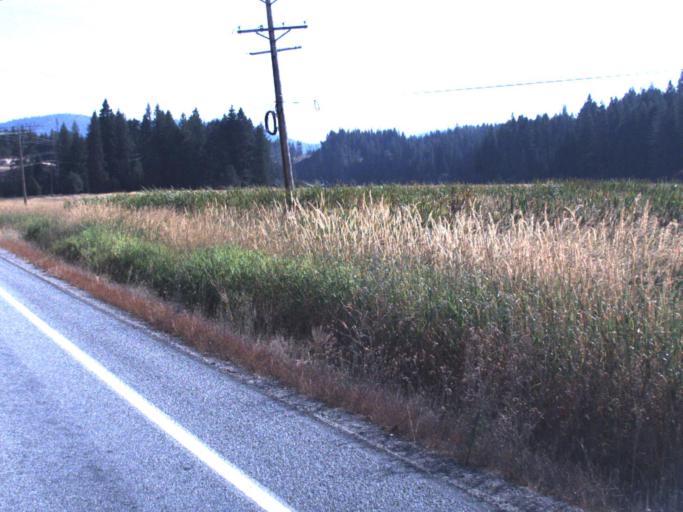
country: US
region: Washington
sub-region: Pend Oreille County
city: Newport
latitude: 48.1314
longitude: -117.2798
